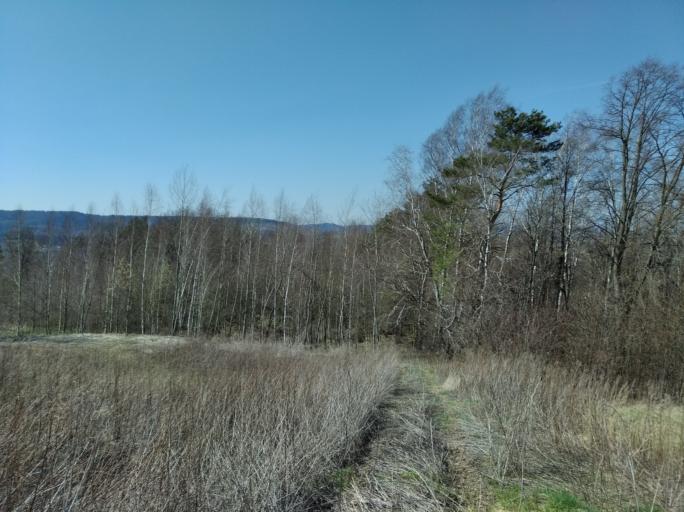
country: PL
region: Subcarpathian Voivodeship
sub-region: Powiat strzyzowski
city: Strzyzow
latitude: 49.8534
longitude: 21.8206
